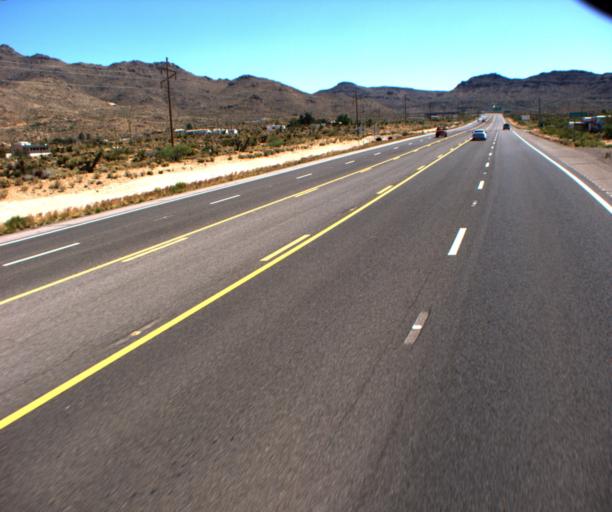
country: US
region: Arizona
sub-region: Mohave County
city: Golden Valley
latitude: 35.2185
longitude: -114.1404
